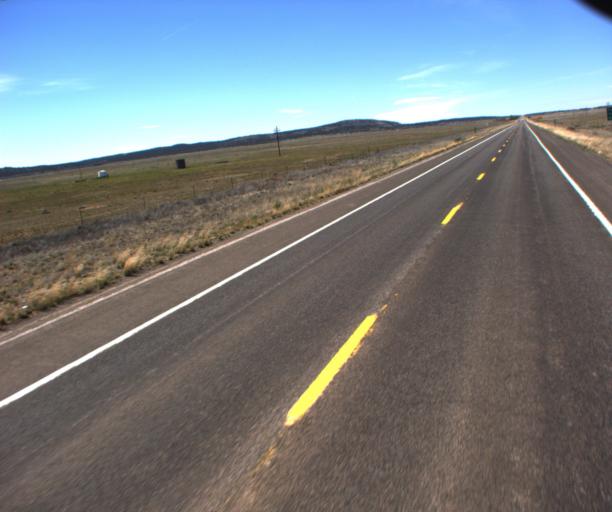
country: US
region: Arizona
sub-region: Mohave County
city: Peach Springs
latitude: 35.4666
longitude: -113.1193
